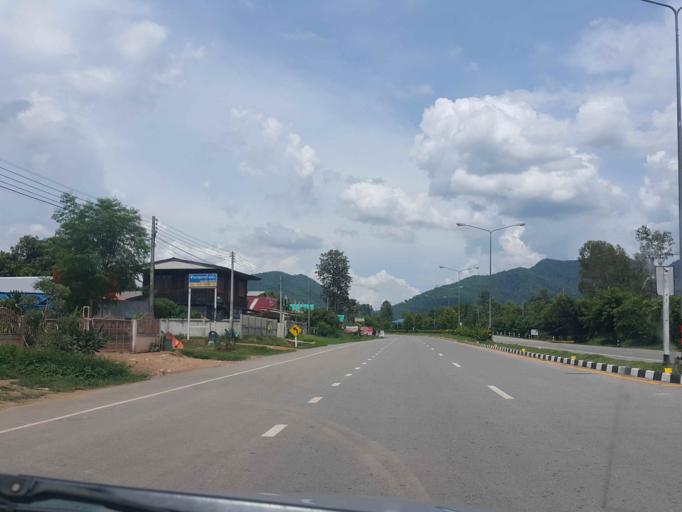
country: TH
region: Nan
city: Ban Luang
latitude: 18.8498
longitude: 100.4413
